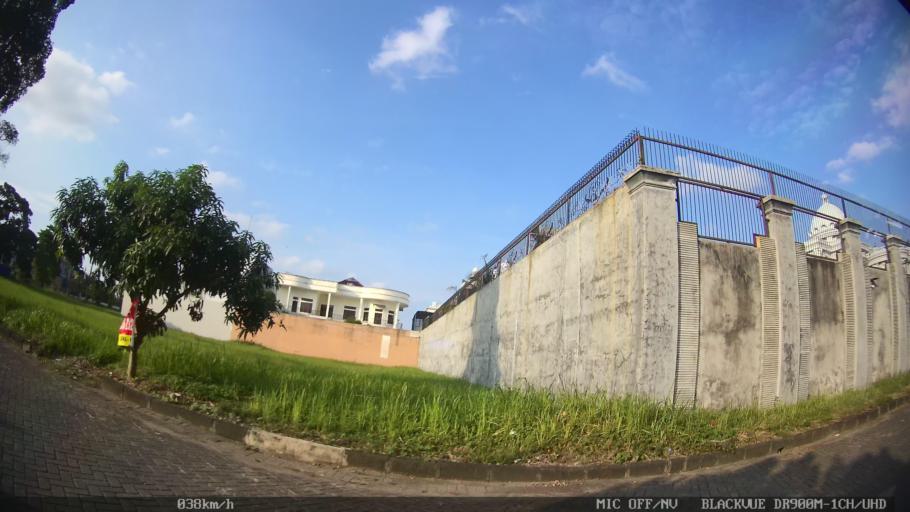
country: ID
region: North Sumatra
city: Medan
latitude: 3.6250
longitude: 98.6520
